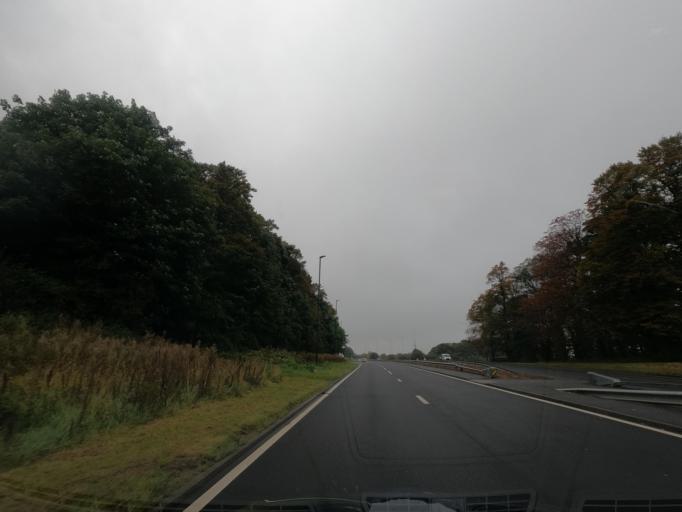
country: GB
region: England
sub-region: Redcar and Cleveland
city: South Bank
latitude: 54.5681
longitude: -1.1163
